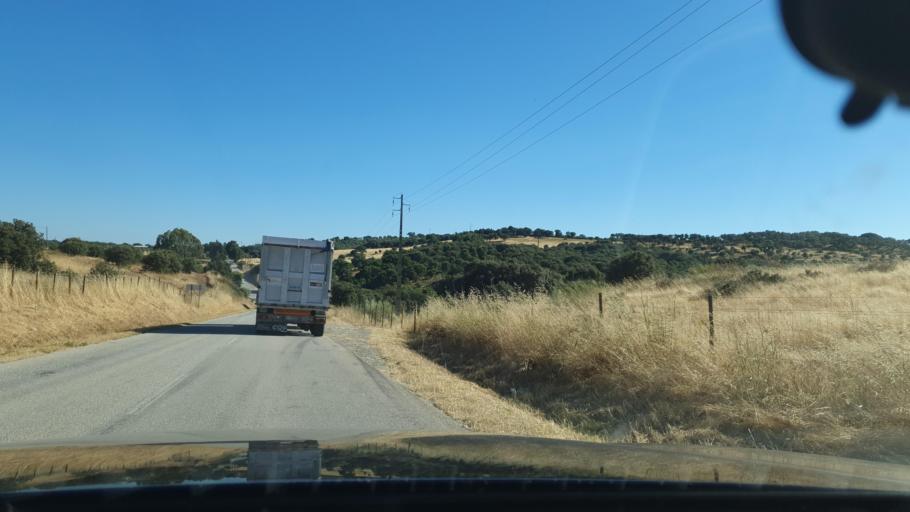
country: PT
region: Evora
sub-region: Alandroal
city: Alandroal
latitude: 38.7229
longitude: -7.4061
